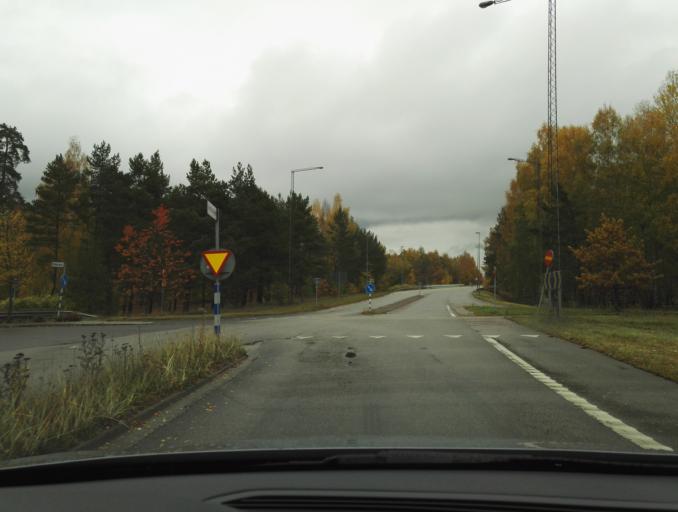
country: SE
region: Kronoberg
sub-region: Vaxjo Kommun
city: Vaexjoe
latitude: 56.8829
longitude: 14.7557
